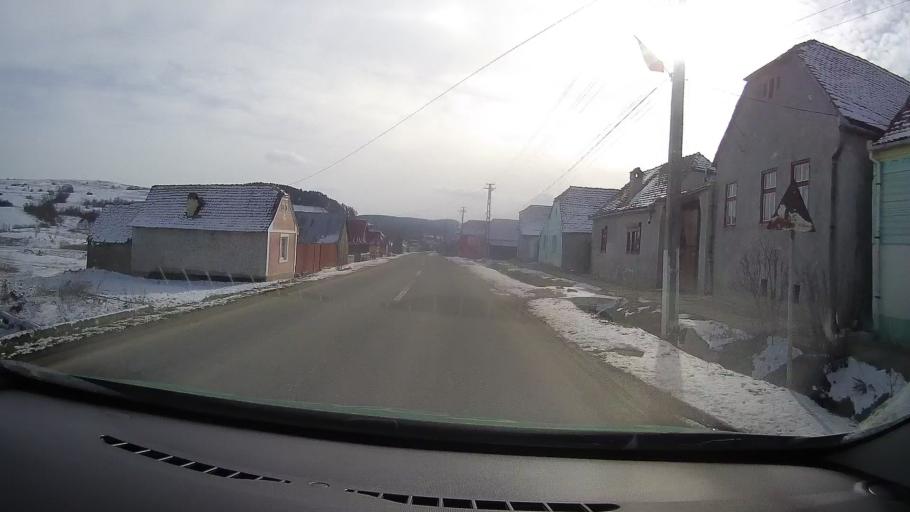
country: RO
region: Sibiu
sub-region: Comuna Bradeni
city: Bradeni
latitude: 46.0879
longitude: 24.8330
